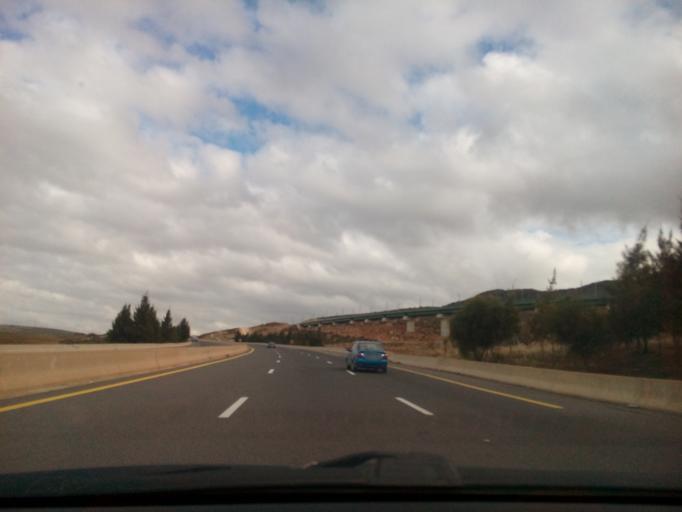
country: DZ
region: Tlemcen
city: Sidi Abdelli
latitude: 35.0098
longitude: -1.1625
